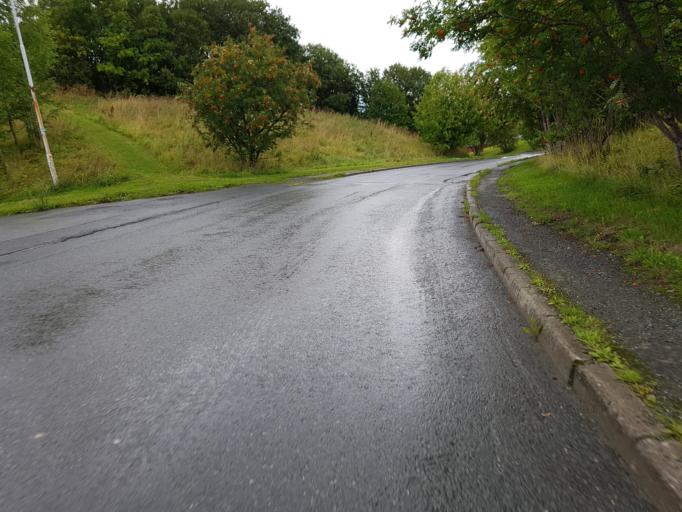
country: NO
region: Sor-Trondelag
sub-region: Trondheim
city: Trondheim
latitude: 63.3953
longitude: 10.4367
